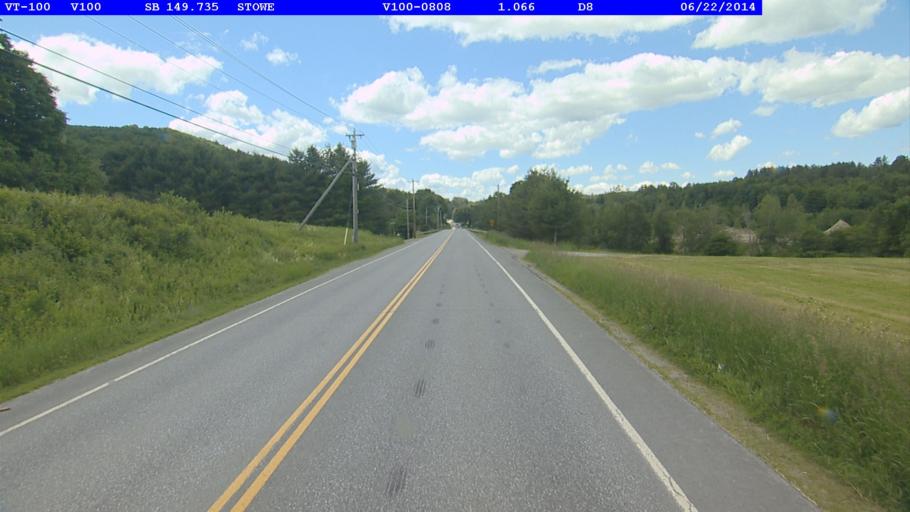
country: US
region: Vermont
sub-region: Washington County
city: Waterbury
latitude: 44.4384
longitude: -72.7099
